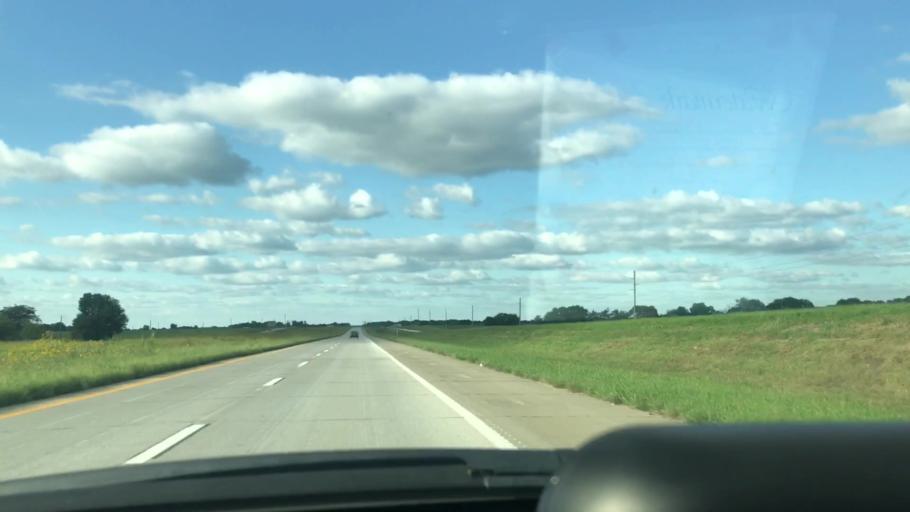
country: US
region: Missouri
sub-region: Benton County
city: Cole Camp
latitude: 38.5091
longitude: -93.2728
